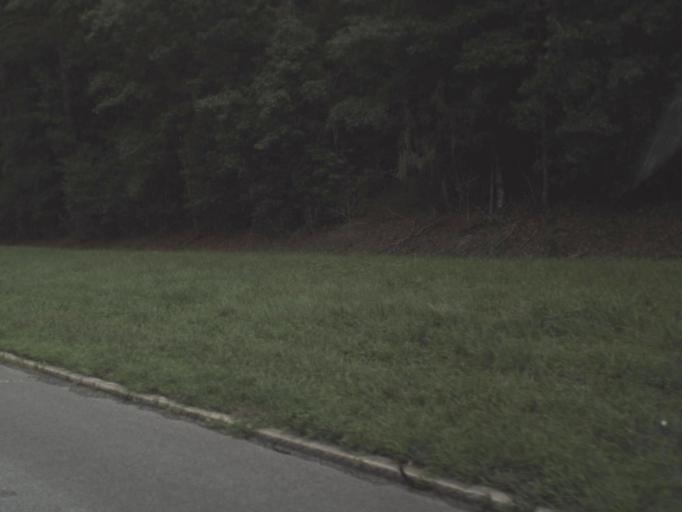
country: US
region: Florida
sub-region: Hernando County
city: Hill 'n Dale
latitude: 28.4647
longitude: -82.2738
